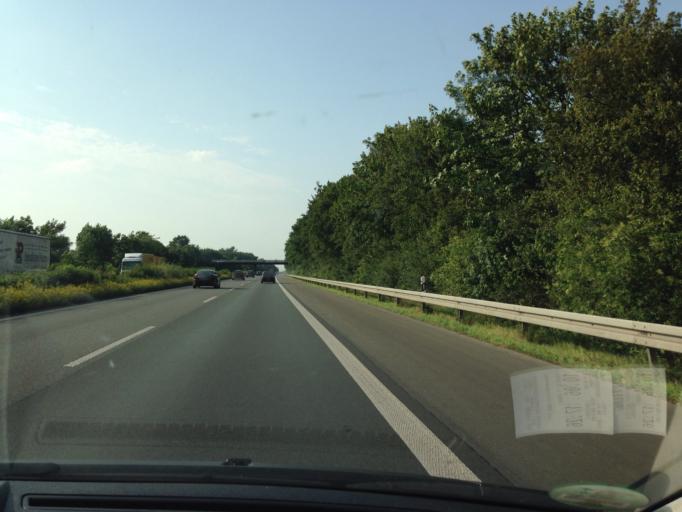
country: DE
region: North Rhine-Westphalia
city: Werne
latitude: 51.7275
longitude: 7.6528
